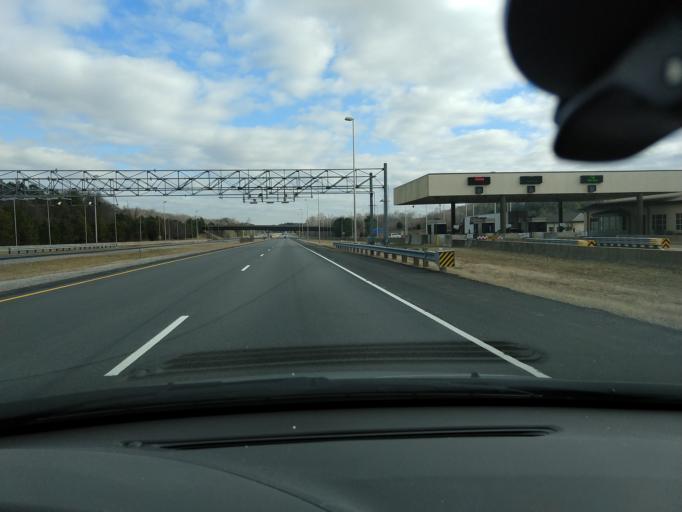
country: US
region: Virginia
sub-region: Chesterfield County
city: Bensley
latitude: 37.4453
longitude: -77.4084
